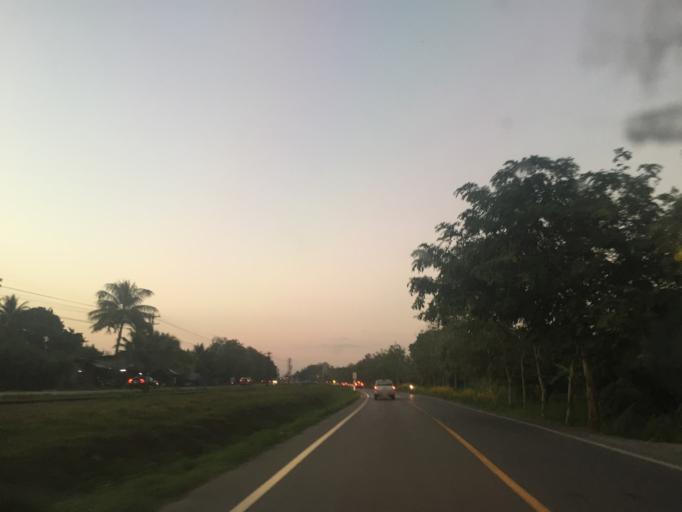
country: TH
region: Chiang Mai
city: Saraphi
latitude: 18.7007
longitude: 99.0457
